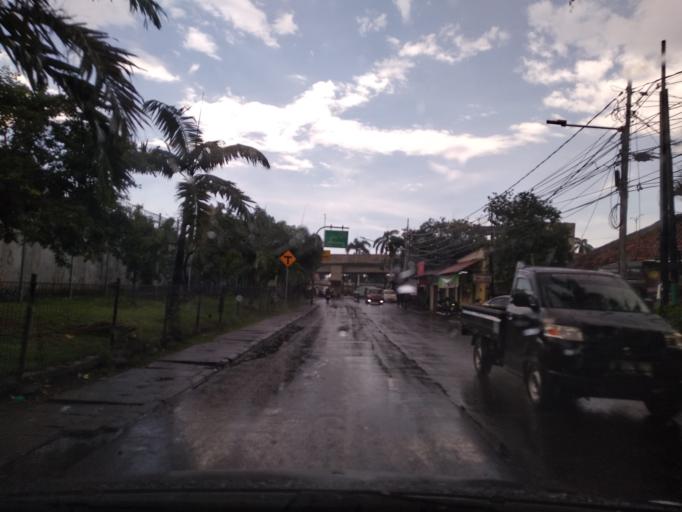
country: ID
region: Jakarta Raya
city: Jakarta
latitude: -6.2153
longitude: 106.8868
